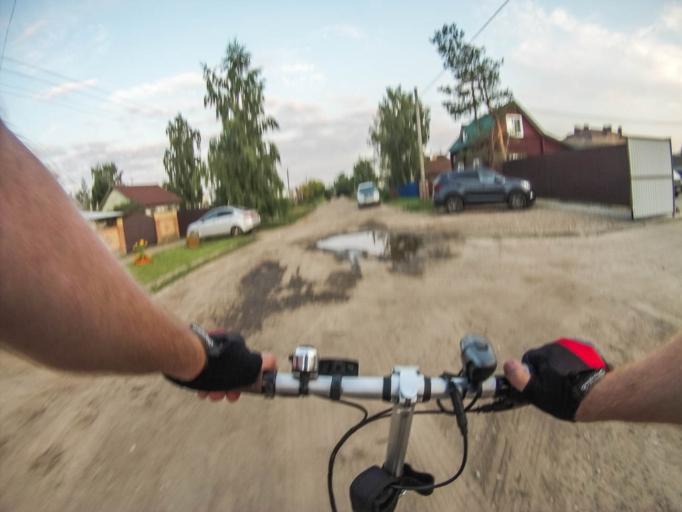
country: RU
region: Kostroma
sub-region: Kostromskoy Rayon
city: Kostroma
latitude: 57.7738
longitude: 40.9561
